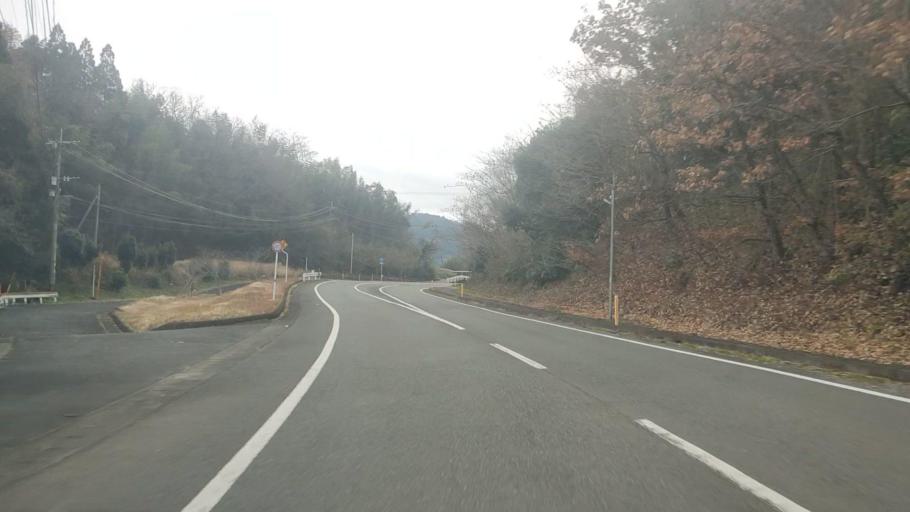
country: JP
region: Kumamoto
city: Ozu
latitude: 32.8606
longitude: 130.8958
